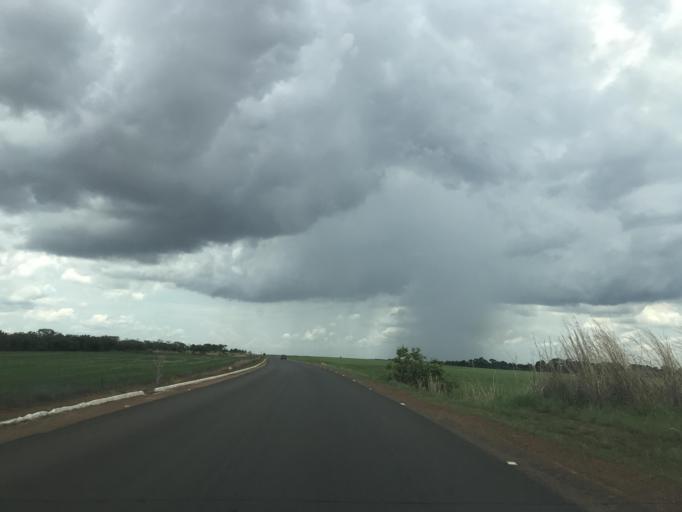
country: BR
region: Goias
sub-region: Vianopolis
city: Vianopolis
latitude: -16.8354
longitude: -48.5331
